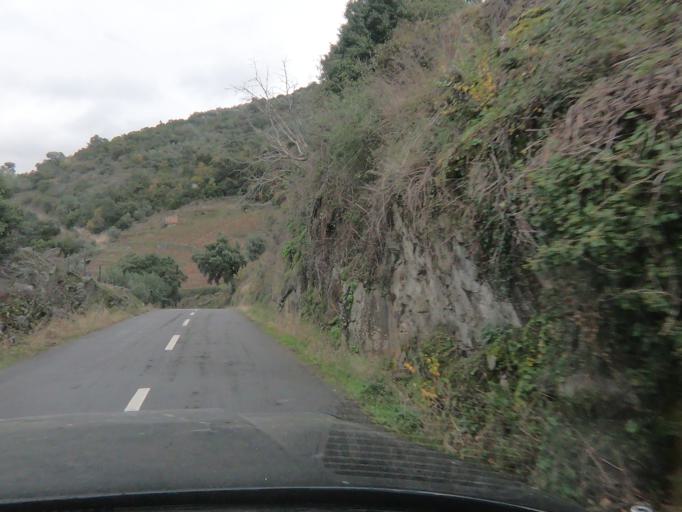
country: PT
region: Vila Real
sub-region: Santa Marta de Penaguiao
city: Santa Marta de Penaguiao
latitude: 41.2159
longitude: -7.7533
